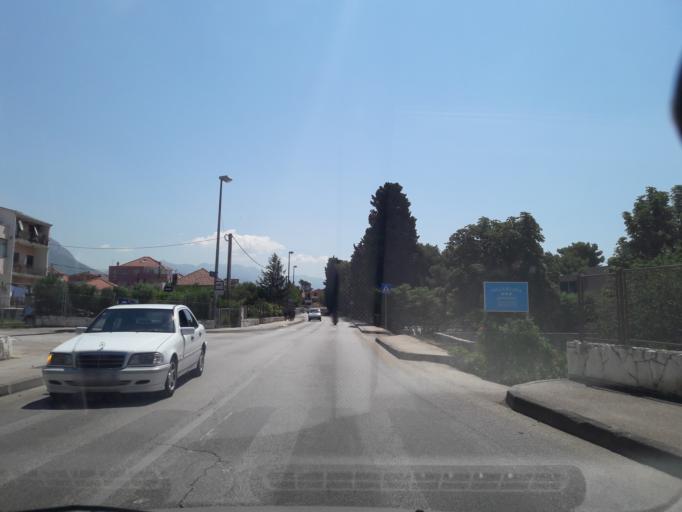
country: HR
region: Splitsko-Dalmatinska
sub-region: Grad Split
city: Split
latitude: 43.5476
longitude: 16.4029
